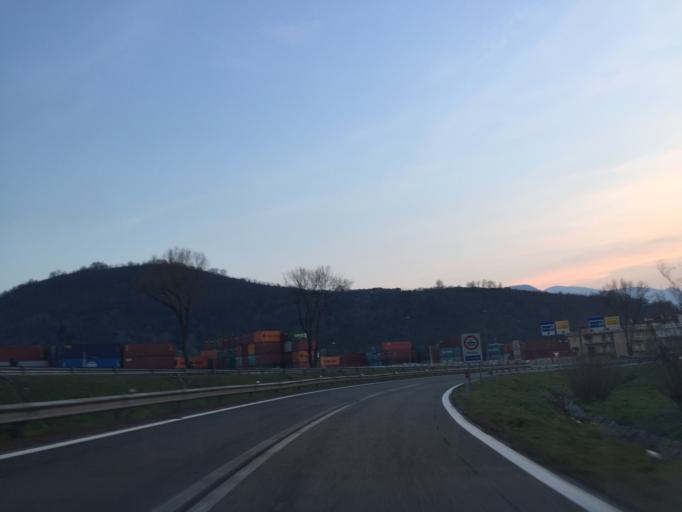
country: IT
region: Campania
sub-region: Provincia di Salerno
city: Lanzara
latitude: 40.7708
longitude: 14.6664
